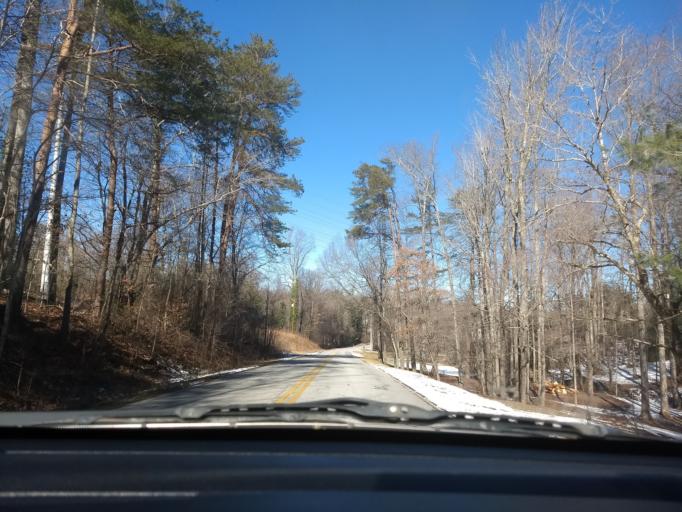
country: US
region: South Carolina
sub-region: Greenville County
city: Wade Hampton
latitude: 34.9191
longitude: -82.3687
